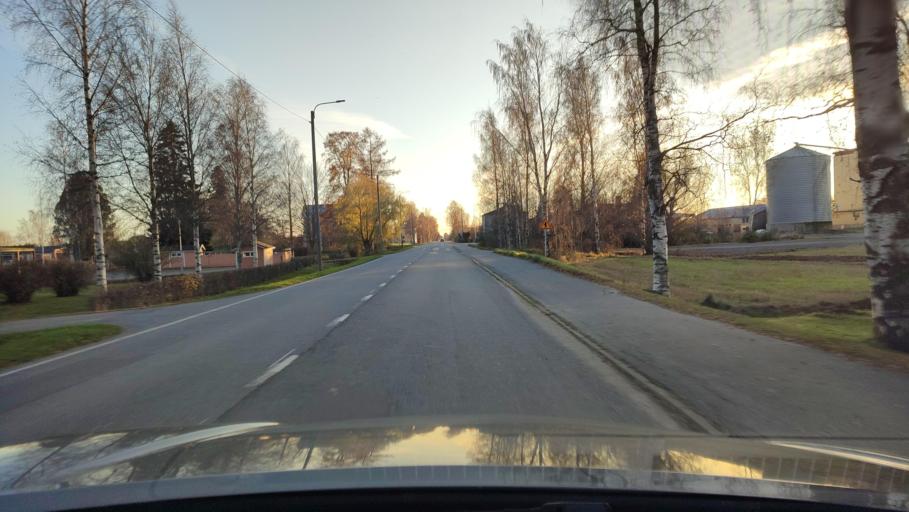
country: FI
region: Ostrobothnia
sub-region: Sydosterbotten
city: Naerpes
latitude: 62.5456
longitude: 21.3972
